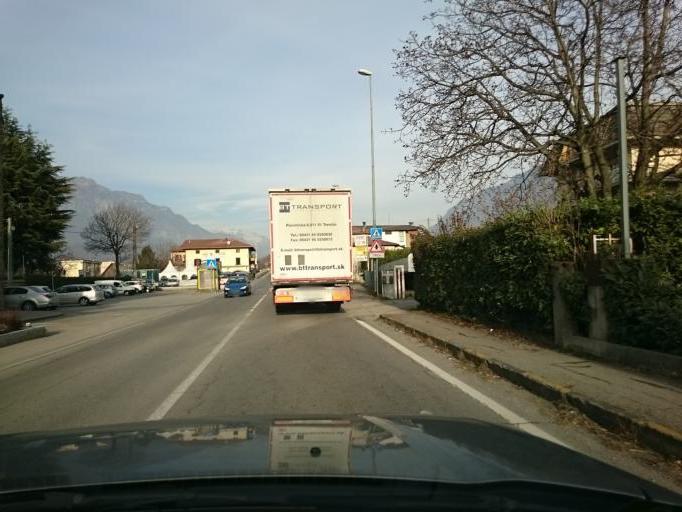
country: IT
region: Lombardy
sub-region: Provincia di Brescia
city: Pian Camuno
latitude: 45.8461
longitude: 10.1455
